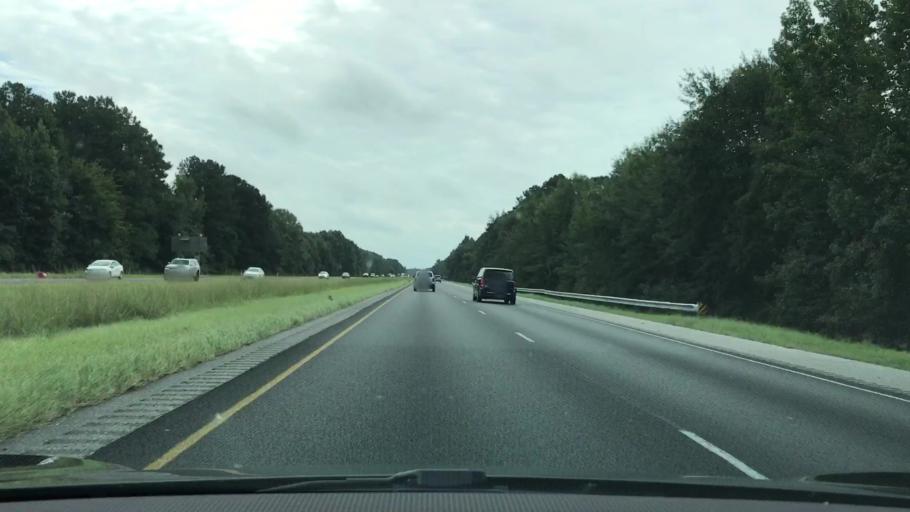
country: US
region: Alabama
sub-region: Montgomery County
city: Pike Road
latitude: 32.3764
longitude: -86.0258
